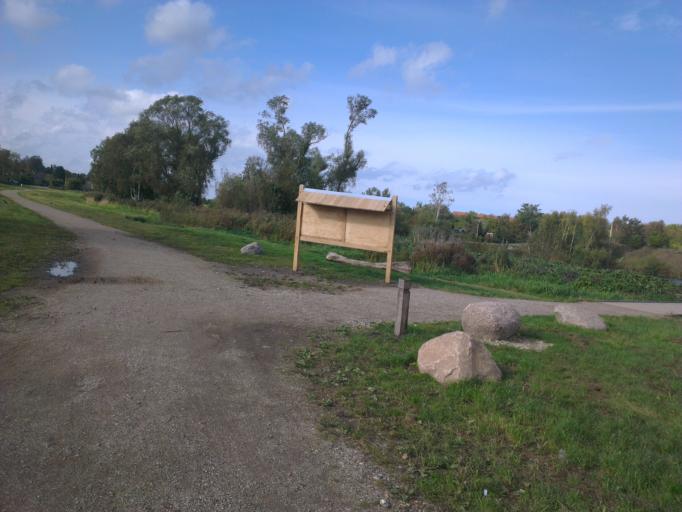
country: DK
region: Capital Region
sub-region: Frederikssund Kommune
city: Frederikssund
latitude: 55.8315
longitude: 12.0898
